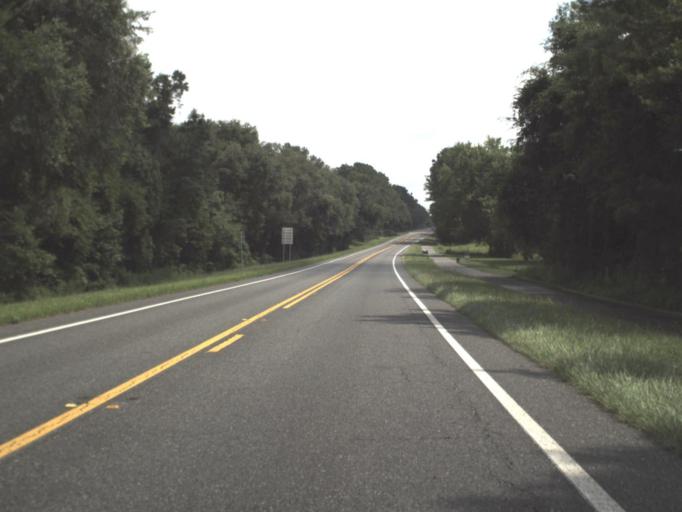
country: US
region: Florida
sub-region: Alachua County
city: High Springs
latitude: 29.9316
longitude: -82.6091
